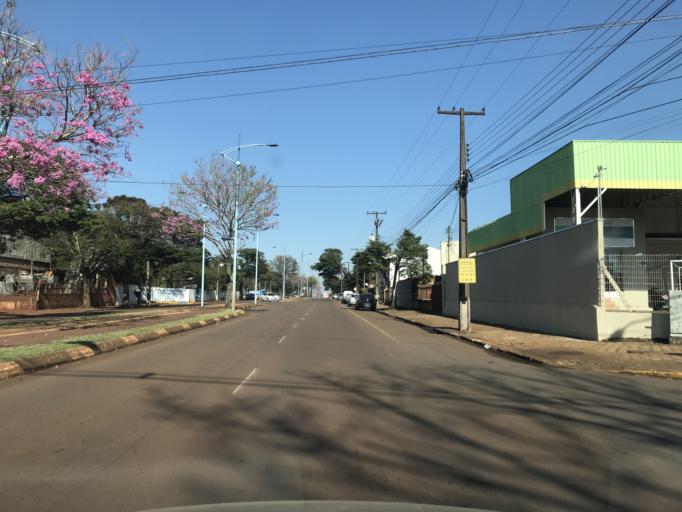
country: BR
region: Parana
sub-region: Toledo
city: Toledo
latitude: -24.7216
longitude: -53.7183
